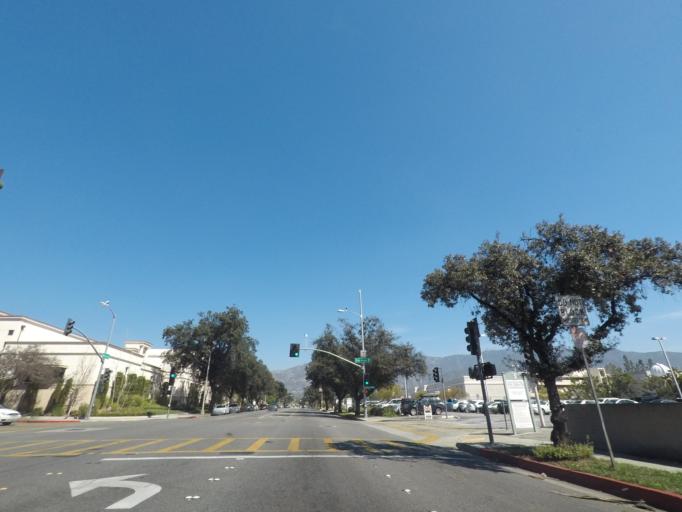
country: US
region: California
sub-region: Los Angeles County
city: Pasadena
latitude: 34.1424
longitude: -118.1213
